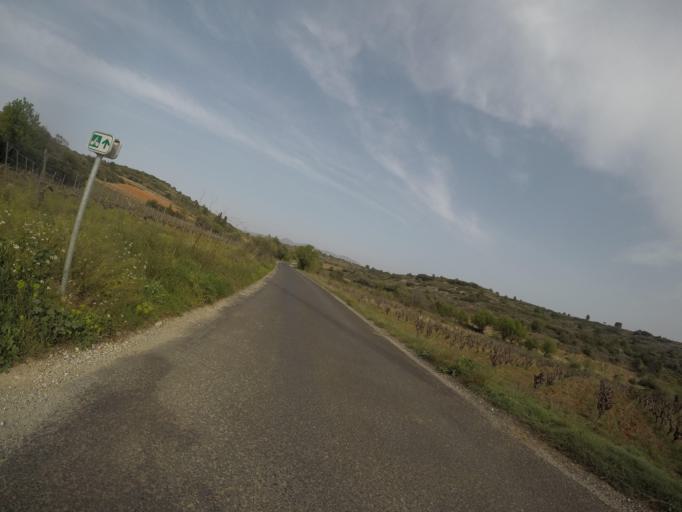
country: FR
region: Languedoc-Roussillon
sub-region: Departement des Pyrenees-Orientales
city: Baixas
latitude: 42.7631
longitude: 2.8184
